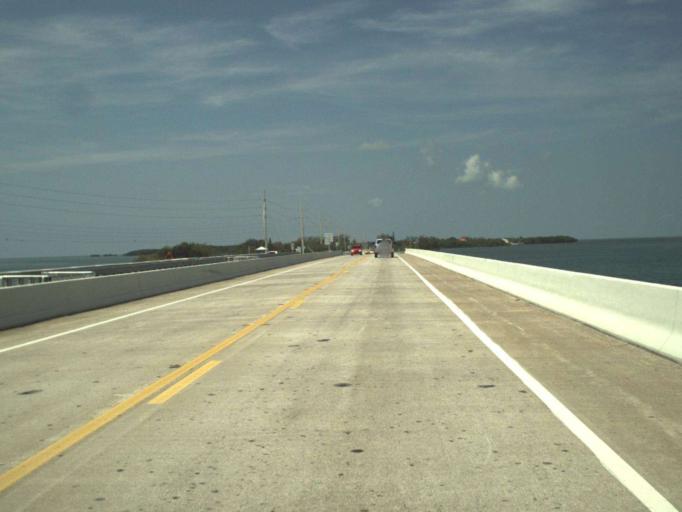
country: US
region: Florida
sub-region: Monroe County
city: Marathon
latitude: 24.7777
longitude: -80.9221
